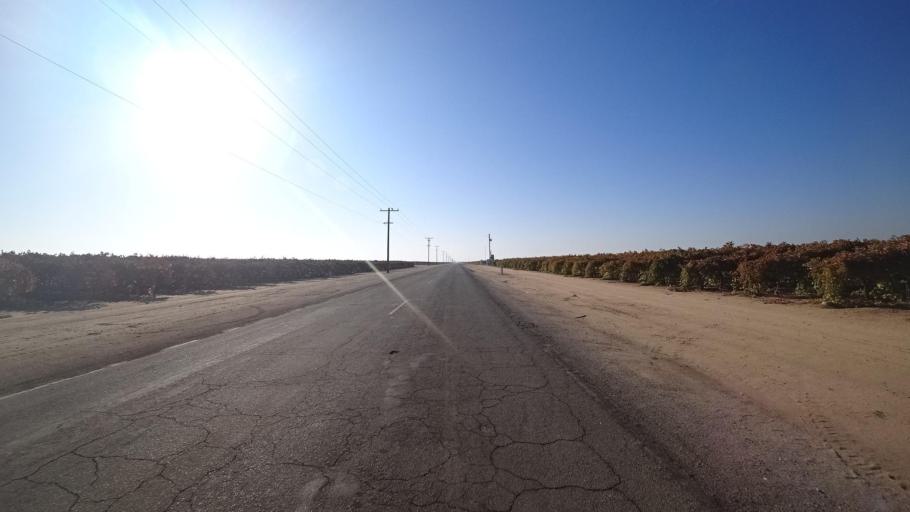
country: US
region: California
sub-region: Tulare County
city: Richgrove
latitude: 35.7555
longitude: -119.1696
